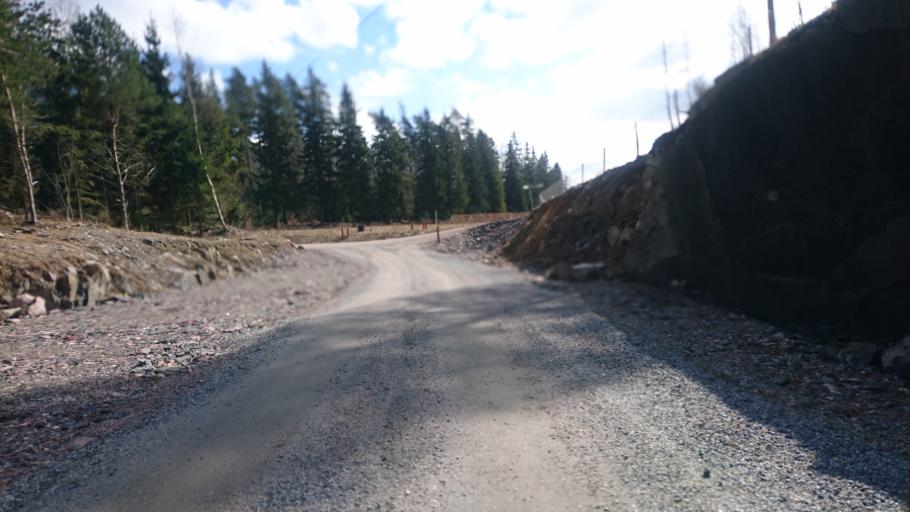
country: FI
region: Uusimaa
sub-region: Helsinki
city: Kauniainen
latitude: 60.1977
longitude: 24.7337
